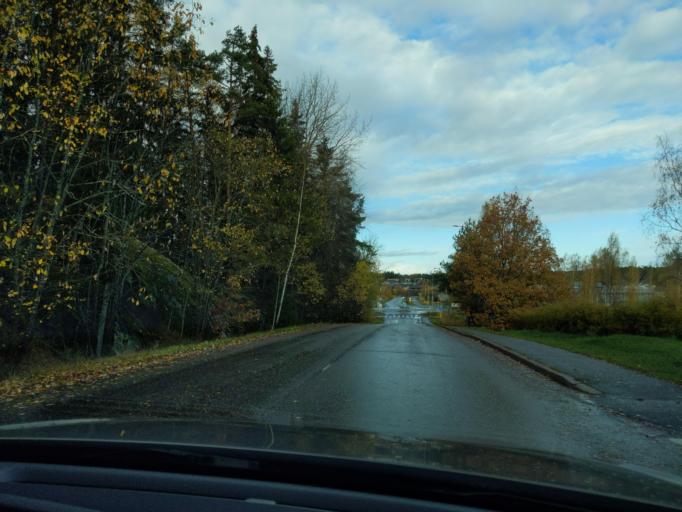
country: FI
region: Varsinais-Suomi
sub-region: Turku
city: Raisio
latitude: 60.4691
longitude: 22.1403
